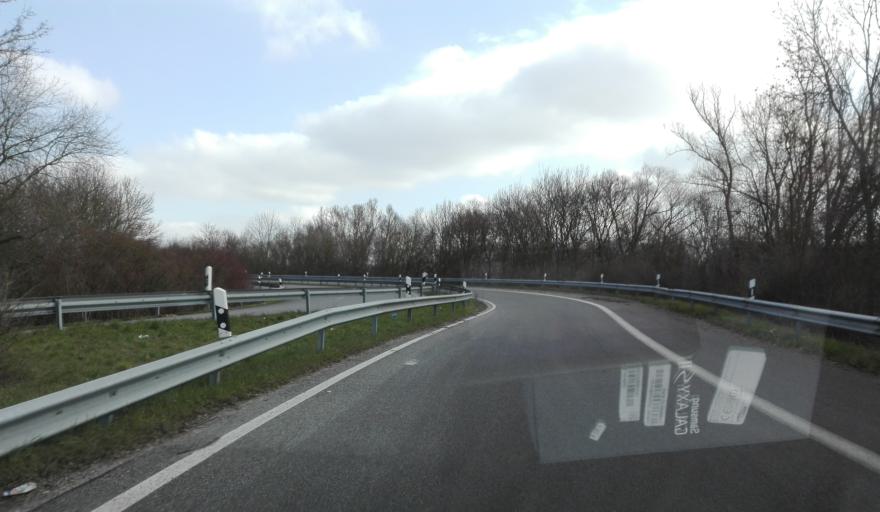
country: DE
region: Rheinland-Pfalz
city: Morstadt
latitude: 49.6647
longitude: 8.2715
